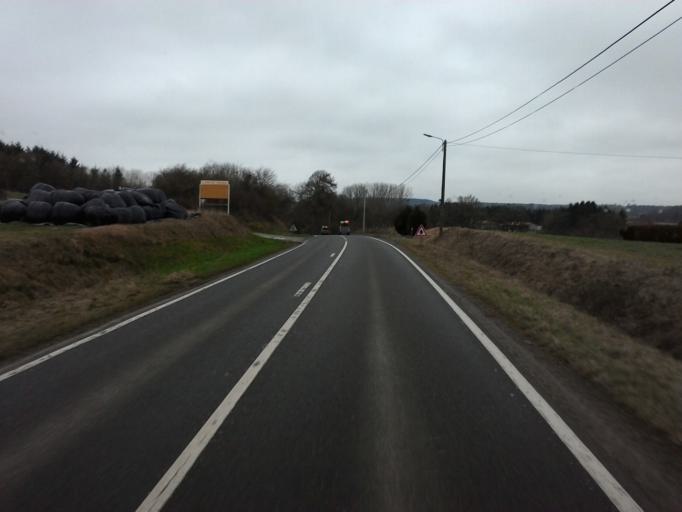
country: BE
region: Wallonia
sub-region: Province de Namur
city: Beauraing
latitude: 50.0948
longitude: 5.0239
